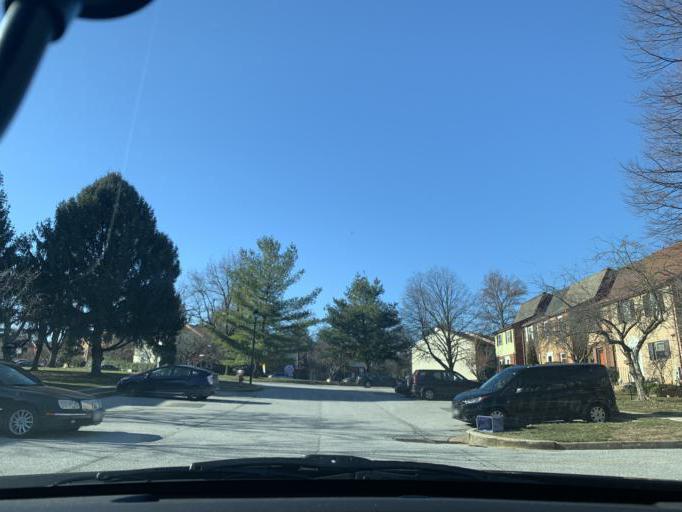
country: US
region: Maryland
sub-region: Baltimore County
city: Garrison
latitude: 39.3996
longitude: -76.7483
